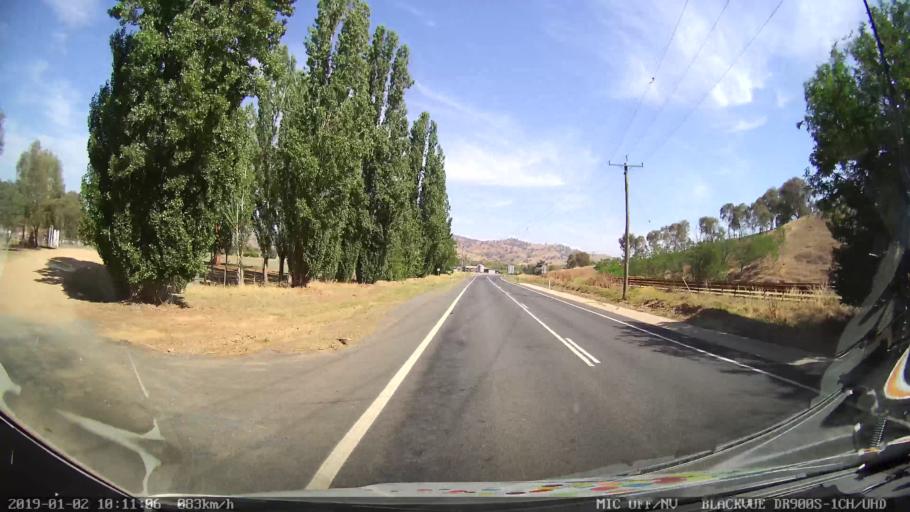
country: AU
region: New South Wales
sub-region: Gundagai
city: Gundagai
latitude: -35.0963
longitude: 148.0930
